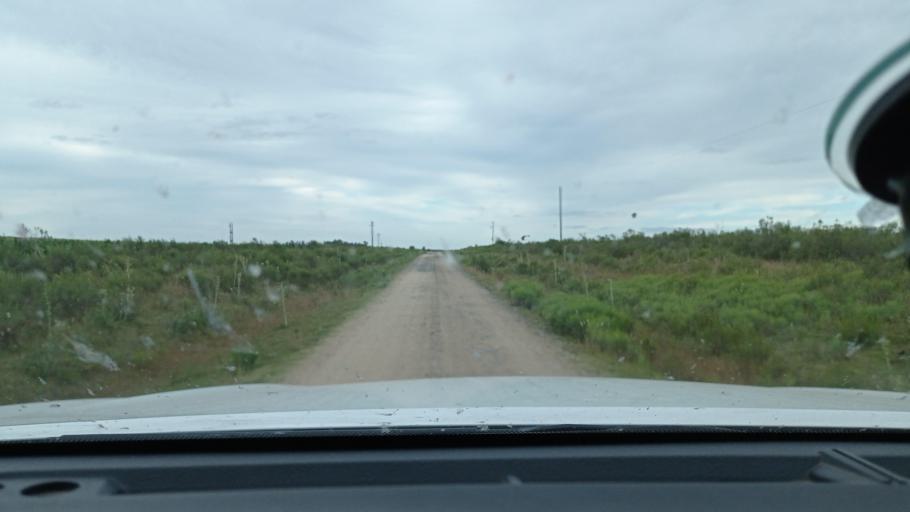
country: UY
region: Florida
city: Casupa
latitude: -34.1265
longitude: -55.7751
